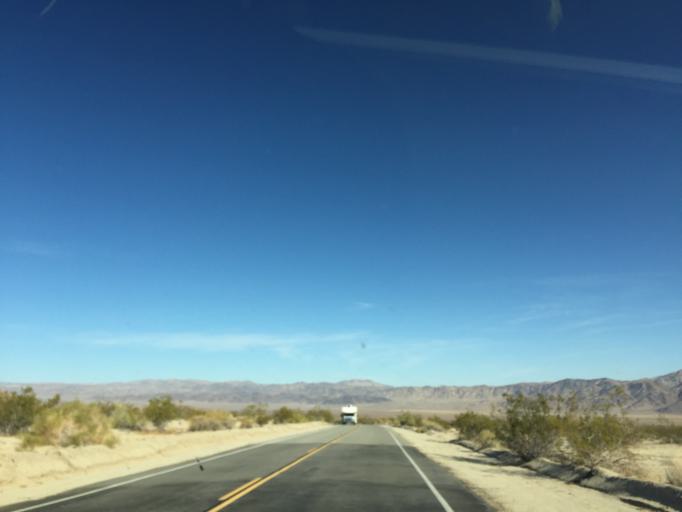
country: US
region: California
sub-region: San Bernardino County
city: Twentynine Palms
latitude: 33.8620
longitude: -115.7950
